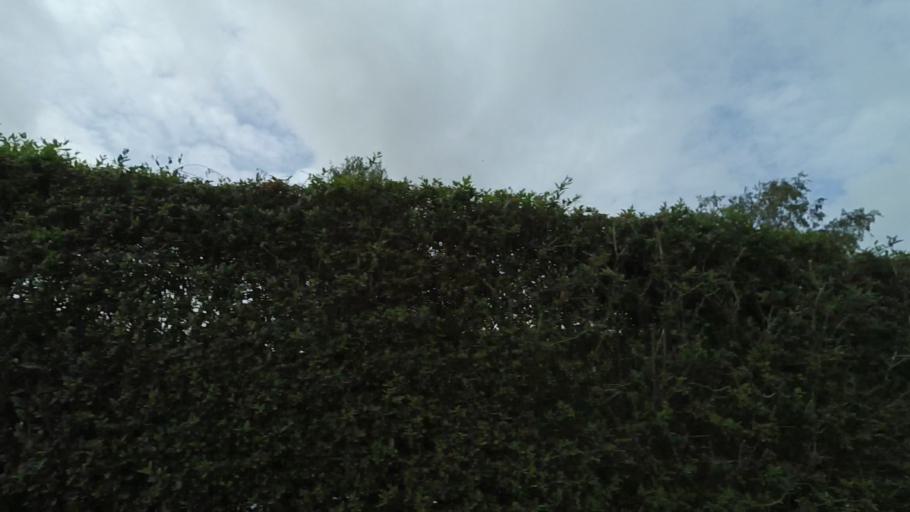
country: DK
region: Central Jutland
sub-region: Syddjurs Kommune
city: Ronde
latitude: 56.3397
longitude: 10.4648
